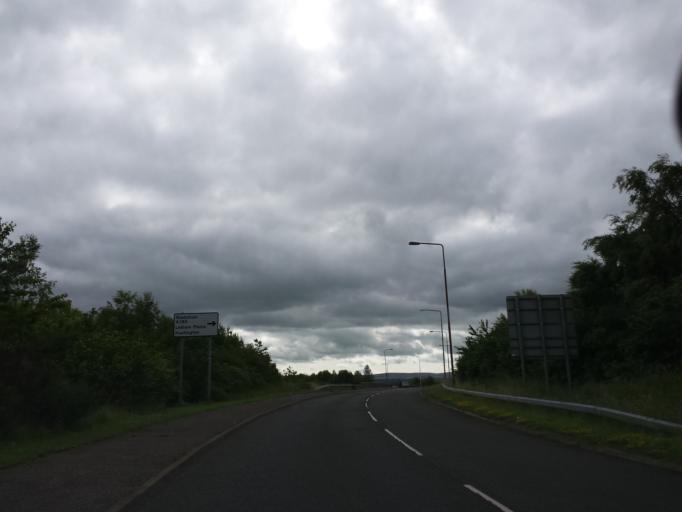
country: GB
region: Scotland
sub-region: East Lothian
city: Haddington
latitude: 55.9553
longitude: -2.8216
